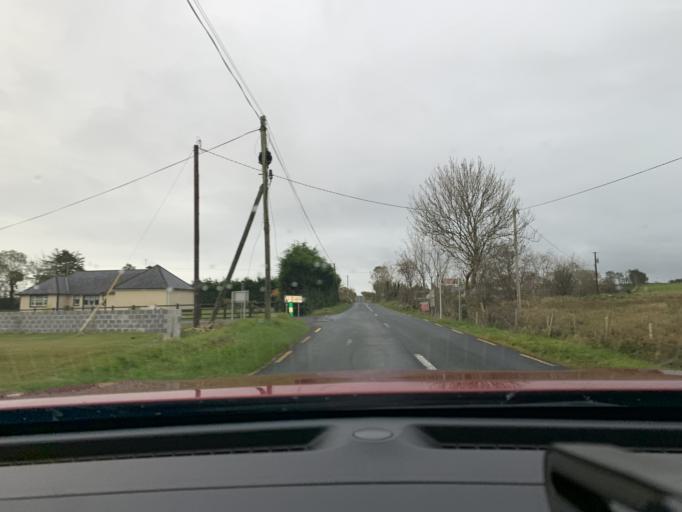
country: IE
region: Connaught
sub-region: Roscommon
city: Ballaghaderreen
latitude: 53.9599
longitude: -8.5419
